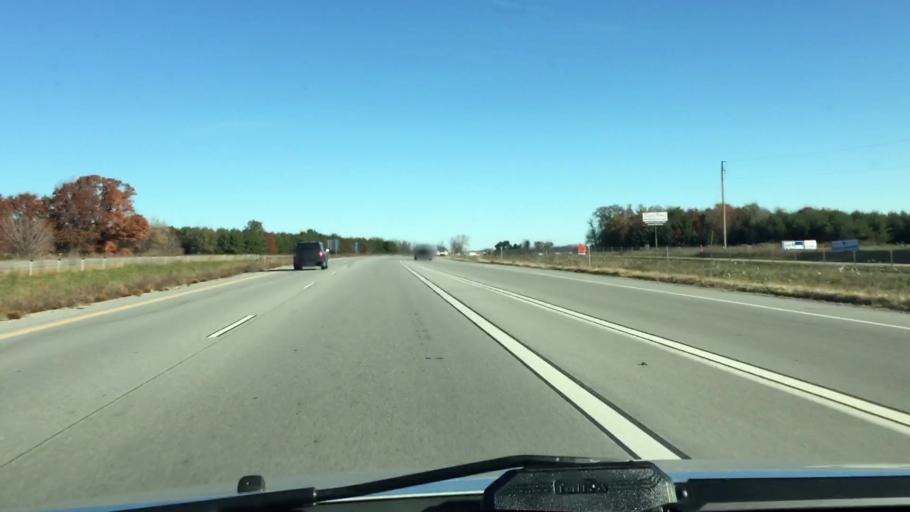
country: US
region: Wisconsin
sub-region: Brown County
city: Wrightstown
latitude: 44.3897
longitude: -88.1605
